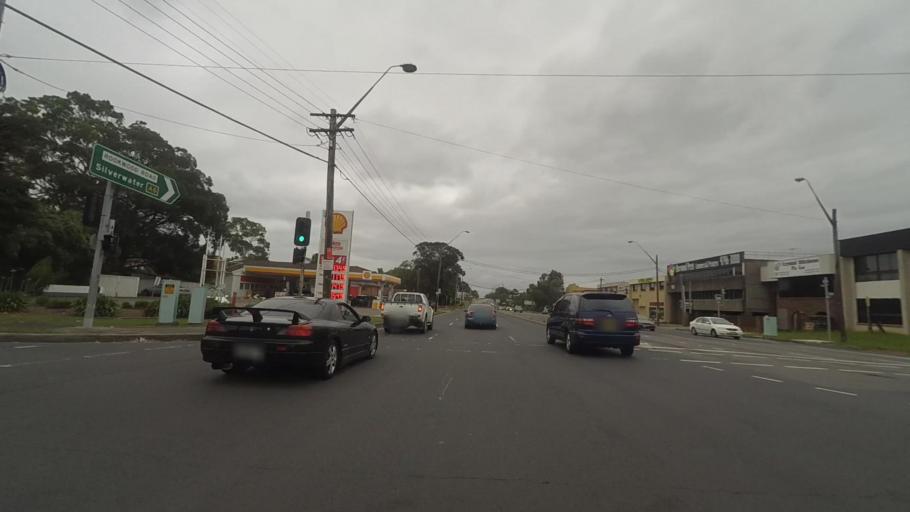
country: AU
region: New South Wales
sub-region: Bankstown
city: Bankstown
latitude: -33.8990
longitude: 151.0372
